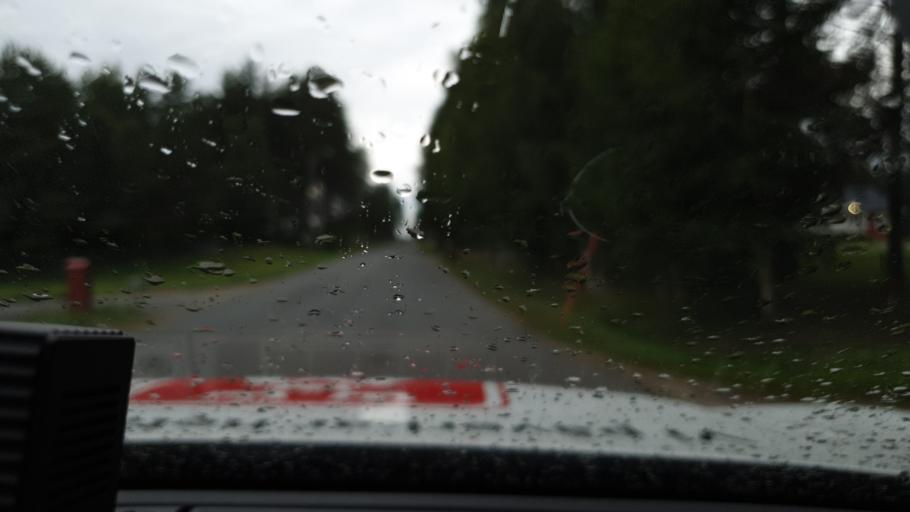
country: SE
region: Norrbotten
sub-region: Lulea Kommun
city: Sodra Sunderbyn
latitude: 65.6740
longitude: 21.8846
